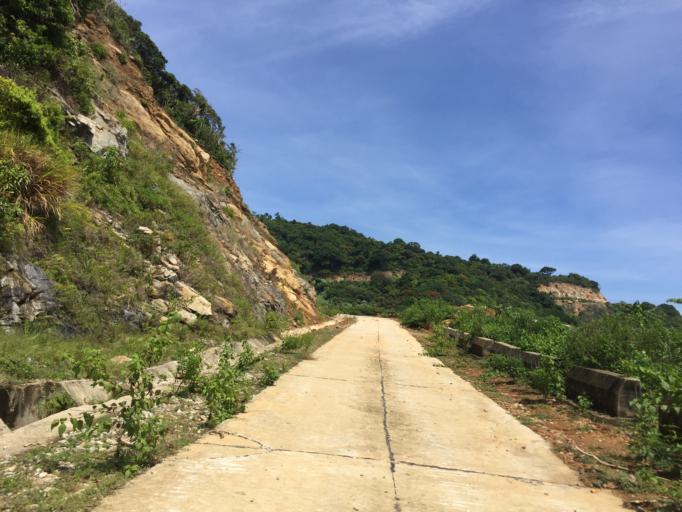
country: VN
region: Quang Nam
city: Hoi An
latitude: 15.9694
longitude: 108.5076
